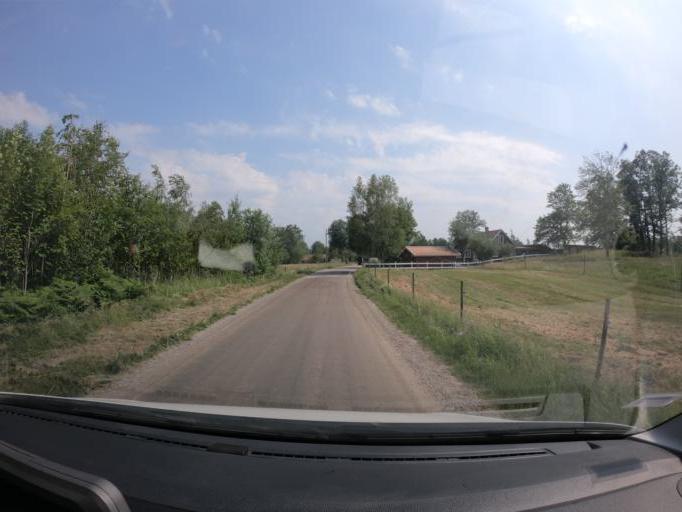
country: SE
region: Kronoberg
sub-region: Markaryds Kommun
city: Markaryd
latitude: 56.3748
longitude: 13.5864
